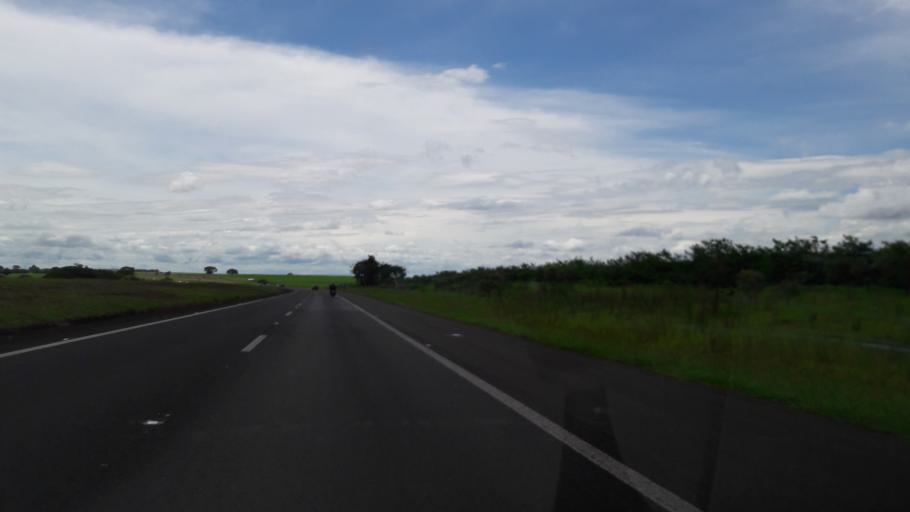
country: BR
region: Sao Paulo
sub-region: Avare
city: Avare
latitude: -22.9422
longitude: -48.9042
